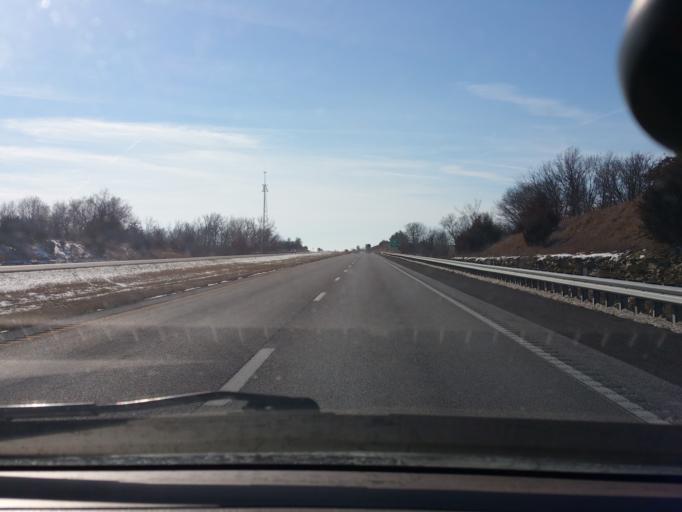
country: US
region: Missouri
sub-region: Clinton County
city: Cameron
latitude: 39.8761
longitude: -94.1659
